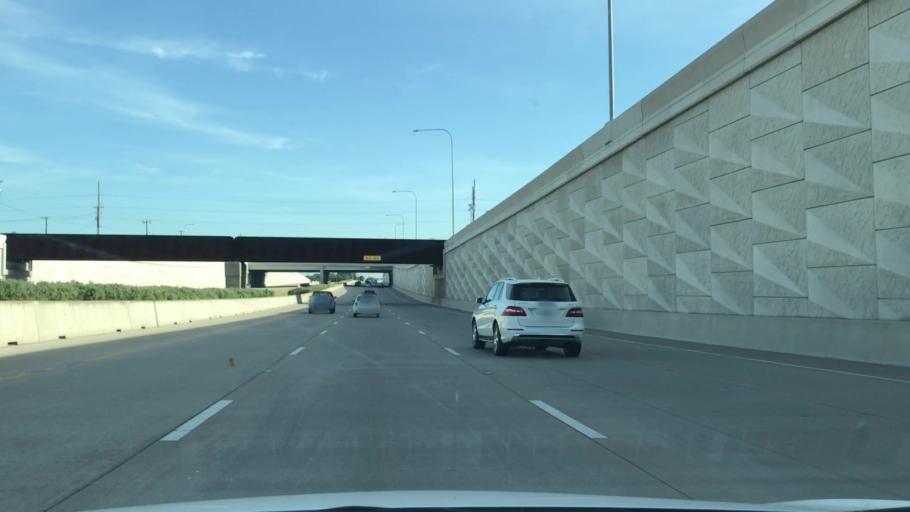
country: US
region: Texas
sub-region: Dallas County
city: Rowlett
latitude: 32.9048
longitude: -96.5557
